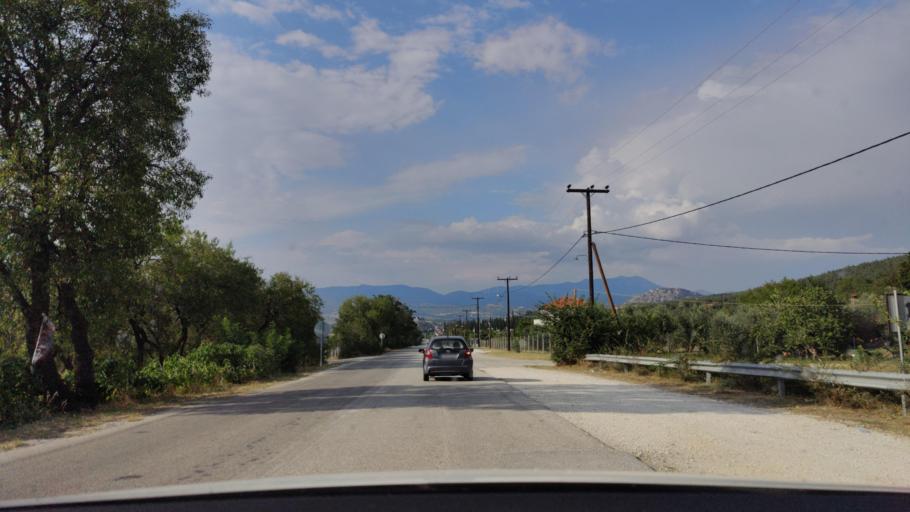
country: GR
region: Central Macedonia
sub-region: Nomos Serron
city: Sidirokastro
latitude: 41.2208
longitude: 23.3899
